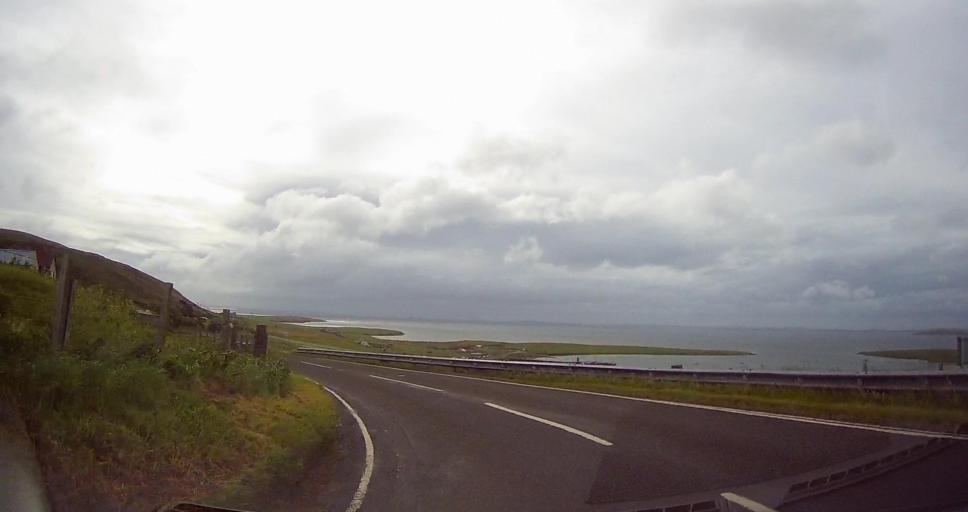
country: GB
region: Scotland
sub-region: Orkney Islands
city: Stromness
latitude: 58.9211
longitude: -3.1968
